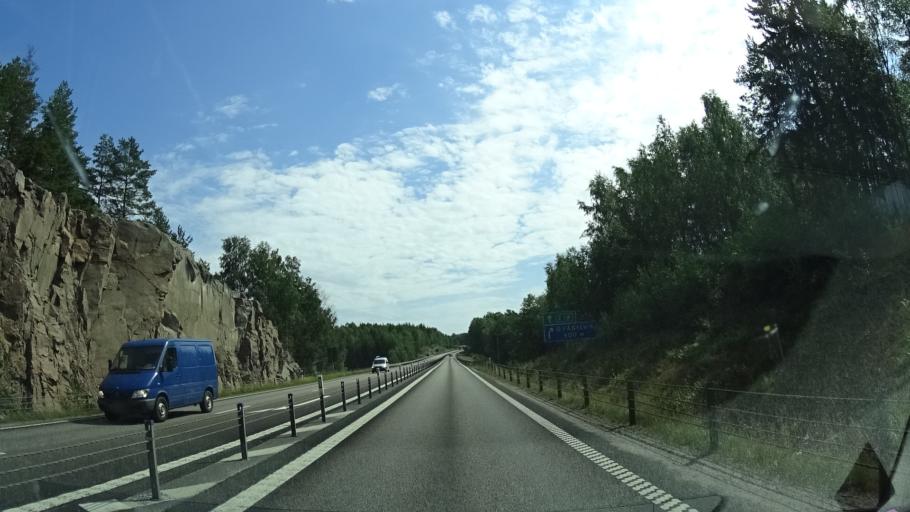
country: SE
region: Vaermland
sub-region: Karlstads Kommun
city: Skattkarr
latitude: 59.4209
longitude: 13.6929
